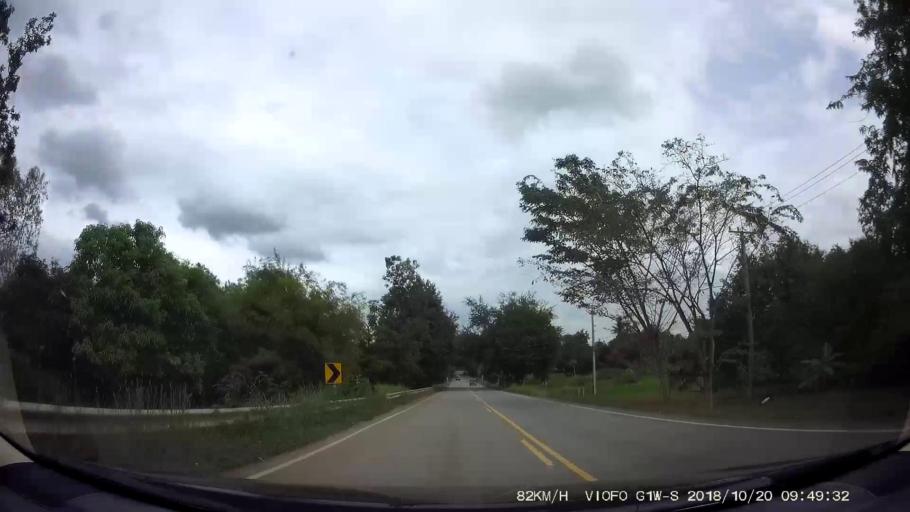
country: TH
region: Chaiyaphum
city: Khon San
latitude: 16.5205
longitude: 101.9049
